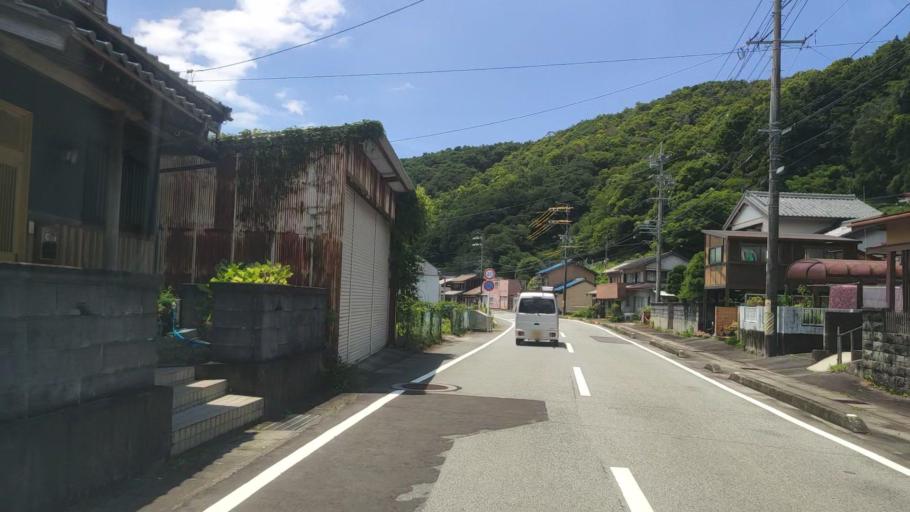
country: JP
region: Mie
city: Owase
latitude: 34.2103
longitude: 136.3499
